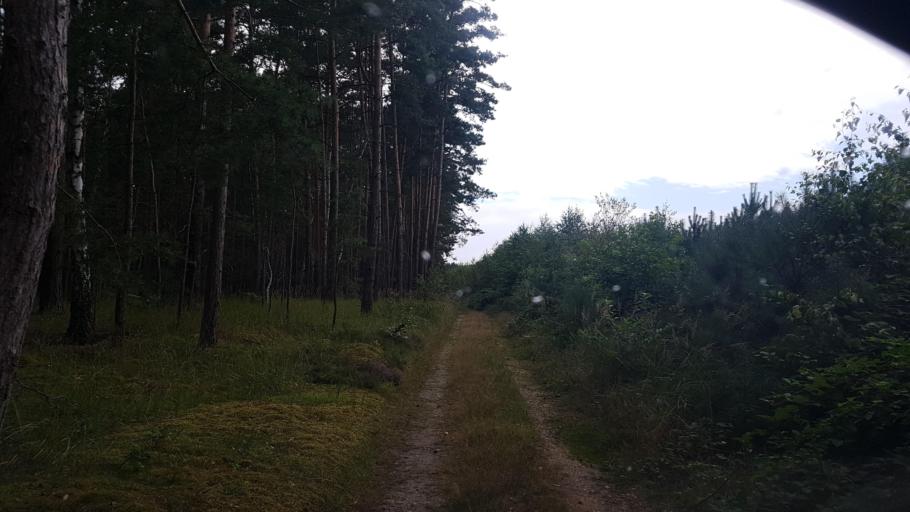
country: DE
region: Brandenburg
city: Sallgast
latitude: 51.5822
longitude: 13.9109
